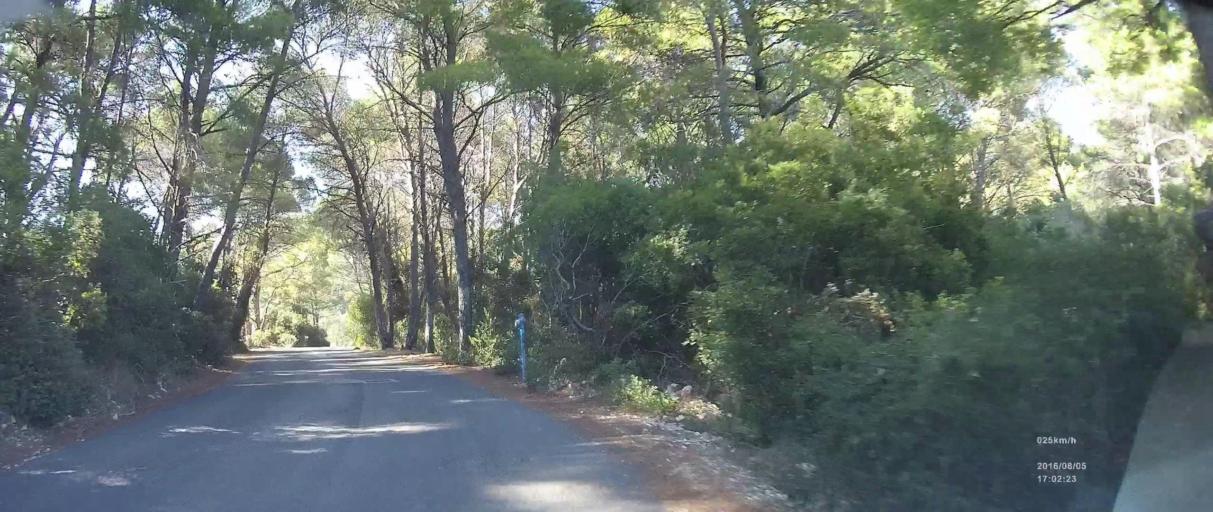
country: HR
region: Dubrovacko-Neretvanska
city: Blato
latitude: 42.7869
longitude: 17.3682
